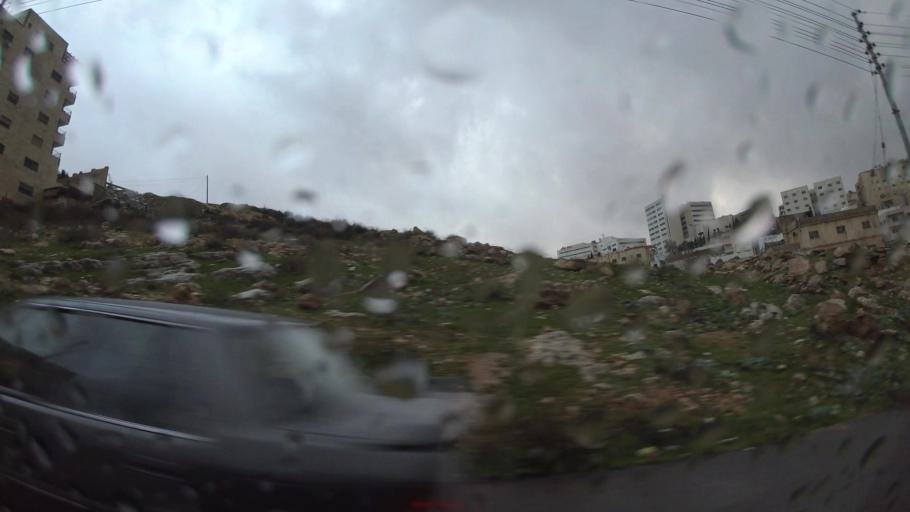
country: JO
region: Amman
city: Amman
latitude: 32.0014
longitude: 35.9232
